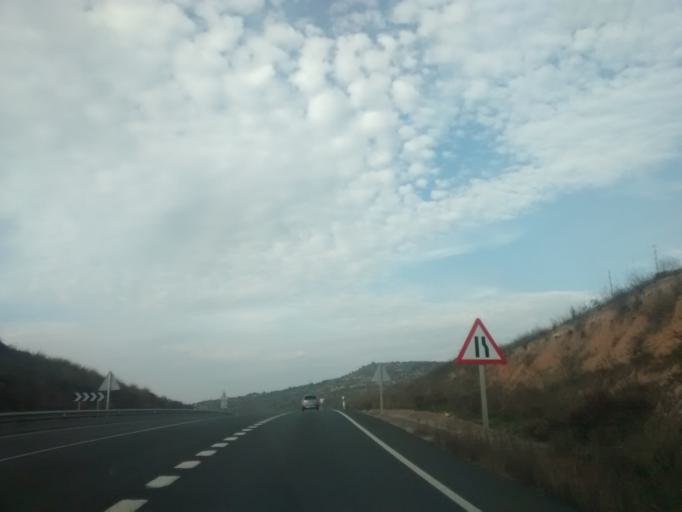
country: ES
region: La Rioja
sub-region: Provincia de La Rioja
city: Cenicero
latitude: 42.4668
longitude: -2.6220
